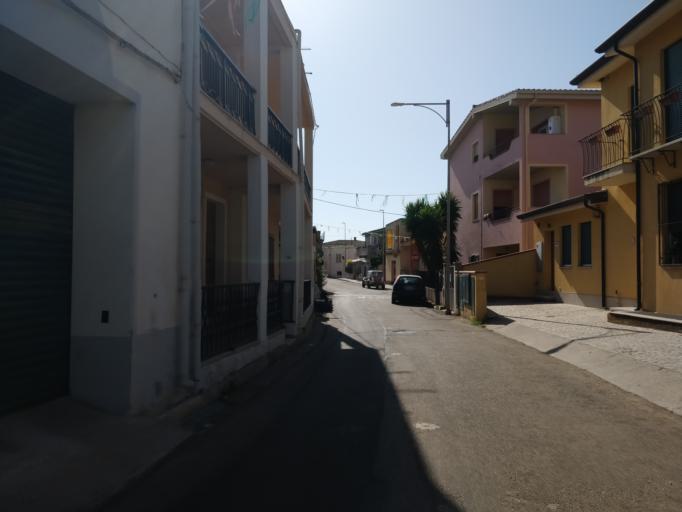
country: IT
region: Sardinia
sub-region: Provincia di Ogliastra
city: Girasole
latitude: 39.9522
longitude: 9.6618
